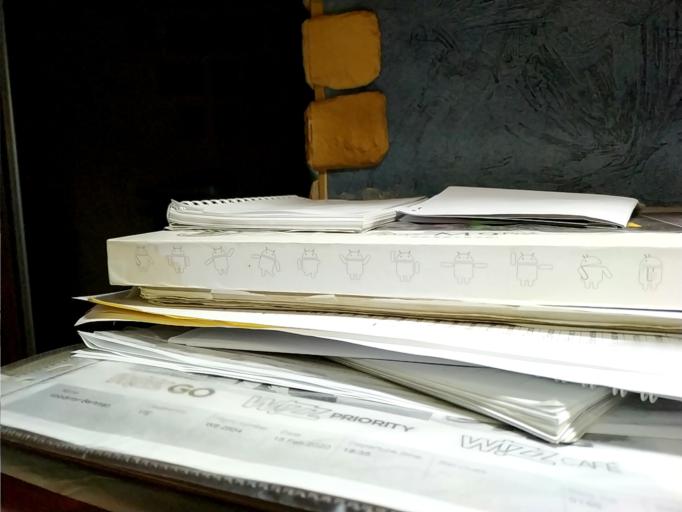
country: RU
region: Arkhangelskaya
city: Onega
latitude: 63.5134
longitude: 38.1378
